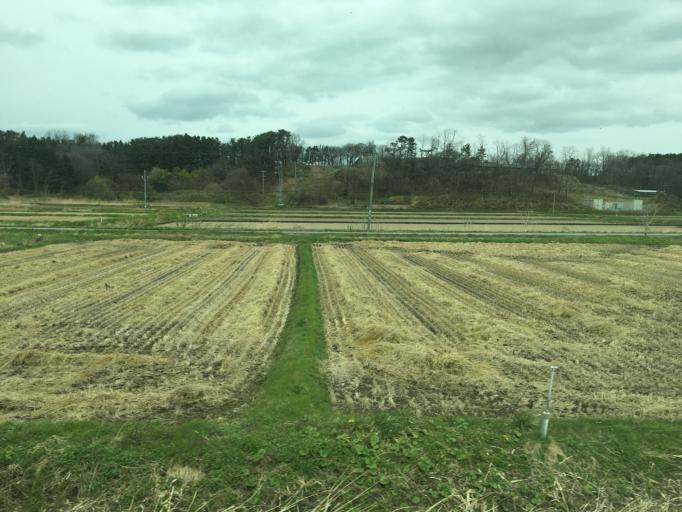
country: JP
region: Aomori
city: Shimokizukuri
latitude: 40.7838
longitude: 140.2568
